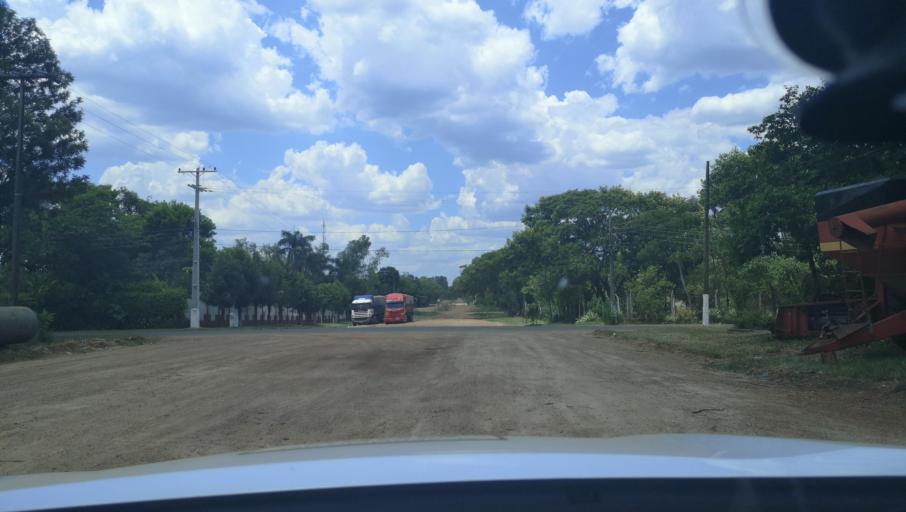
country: PY
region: Itapua
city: Carmen del Parana
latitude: -27.1544
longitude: -56.2480
